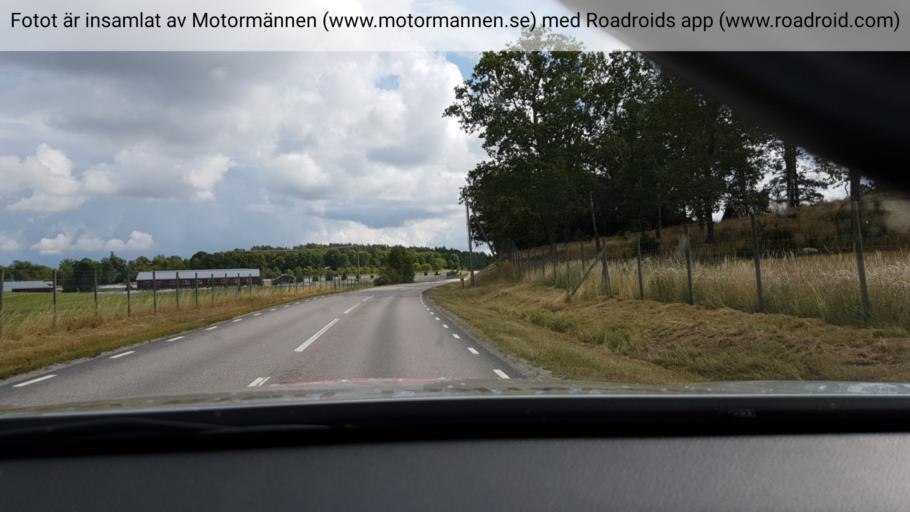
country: SE
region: Stockholm
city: Stenhamra
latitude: 59.3478
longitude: 17.6280
